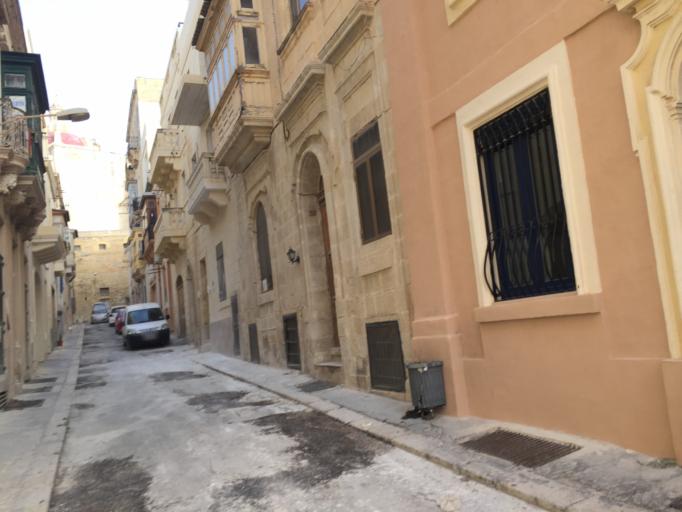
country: MT
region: L-Isla
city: Senglea
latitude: 35.8902
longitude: 14.5146
